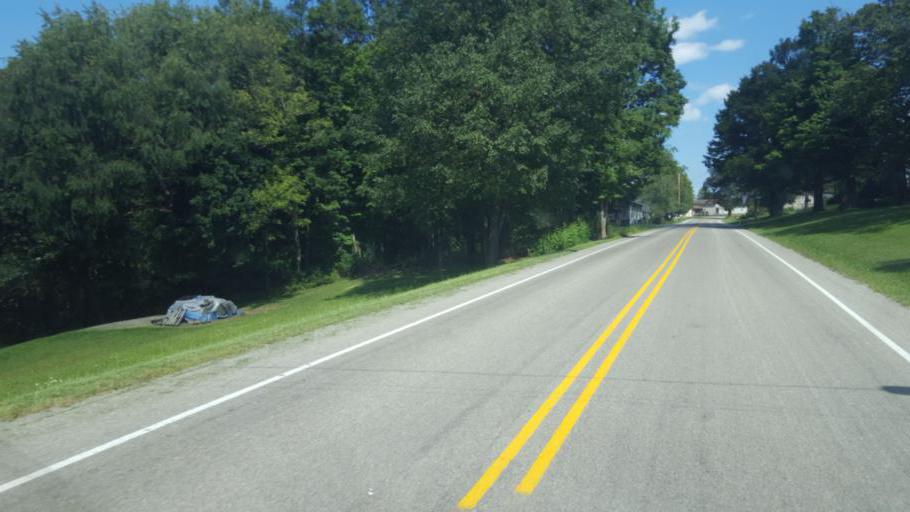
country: US
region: Pennsylvania
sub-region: Clarion County
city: Knox
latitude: 41.1256
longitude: -79.5641
